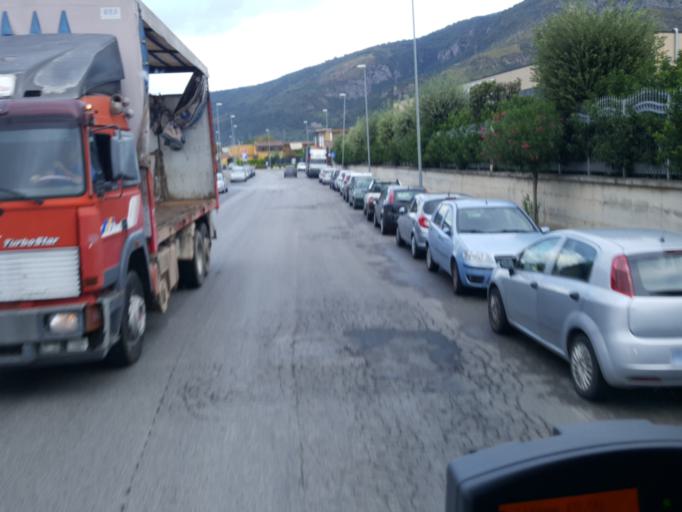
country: IT
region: Campania
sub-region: Provincia di Salerno
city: Sarno
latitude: 40.8212
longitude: 14.6002
